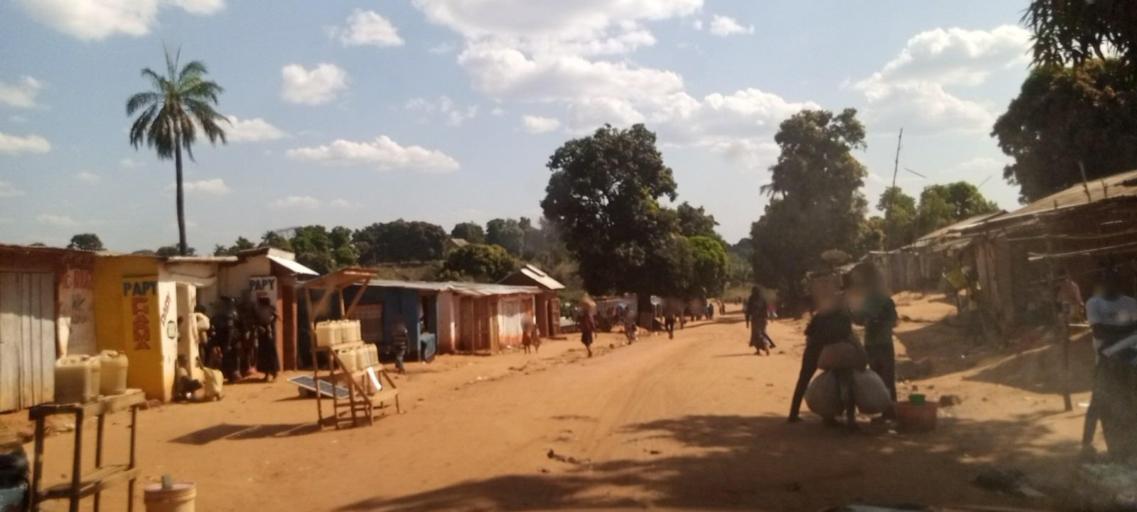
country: CD
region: Kasai-Oriental
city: Kabinda
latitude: -6.1283
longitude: 24.4978
